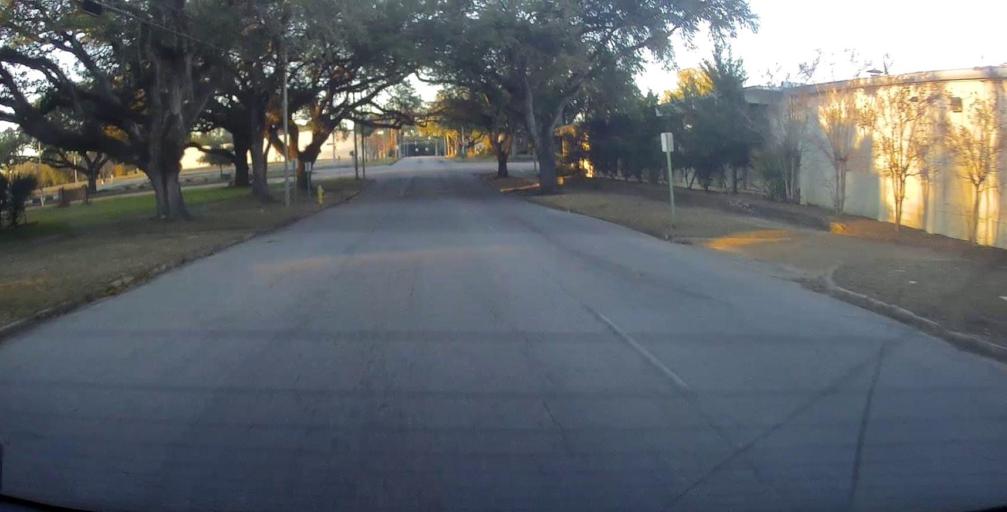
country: US
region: Georgia
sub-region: Dougherty County
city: Albany
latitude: 31.5763
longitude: -84.1617
